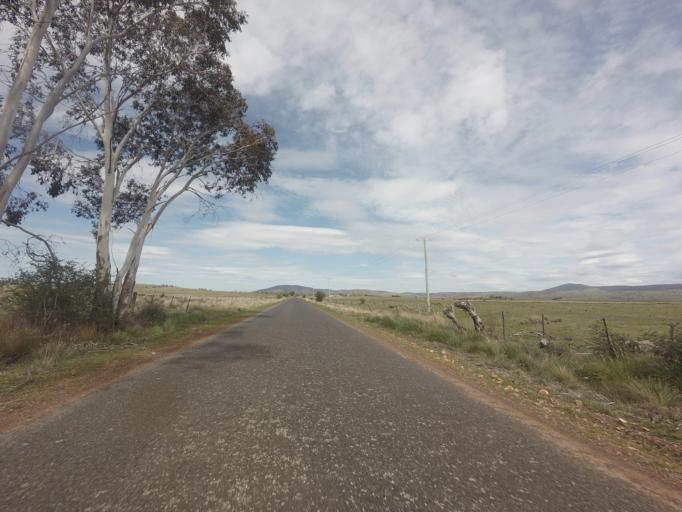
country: AU
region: Tasmania
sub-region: Northern Midlands
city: Evandale
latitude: -41.8670
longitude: 147.3500
